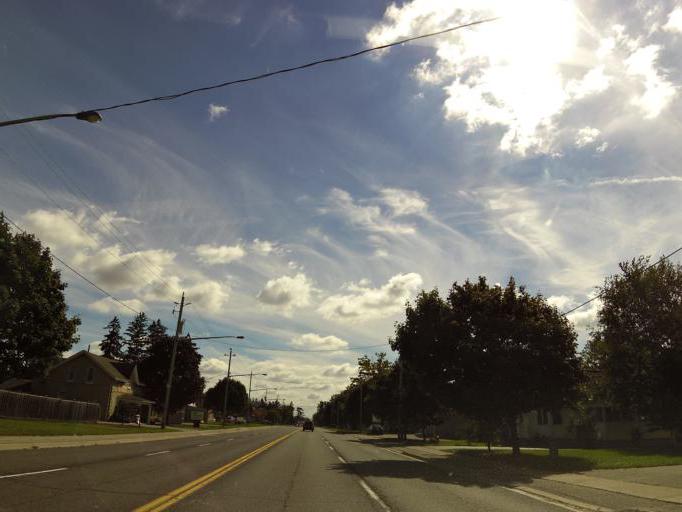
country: CA
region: Ontario
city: London
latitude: 42.9050
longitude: -81.2980
